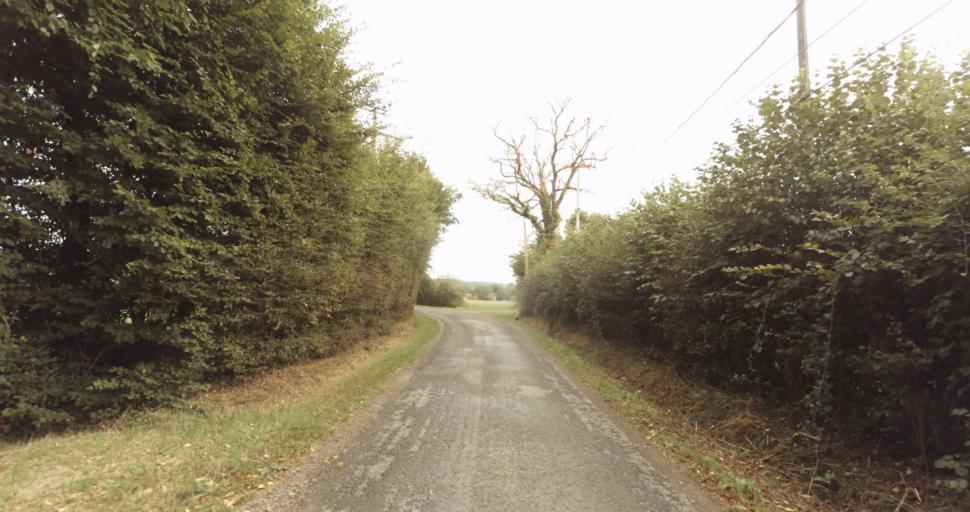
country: FR
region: Lower Normandy
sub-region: Departement de l'Orne
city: Sainte-Gauburge-Sainte-Colombe
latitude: 48.7235
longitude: 0.4785
